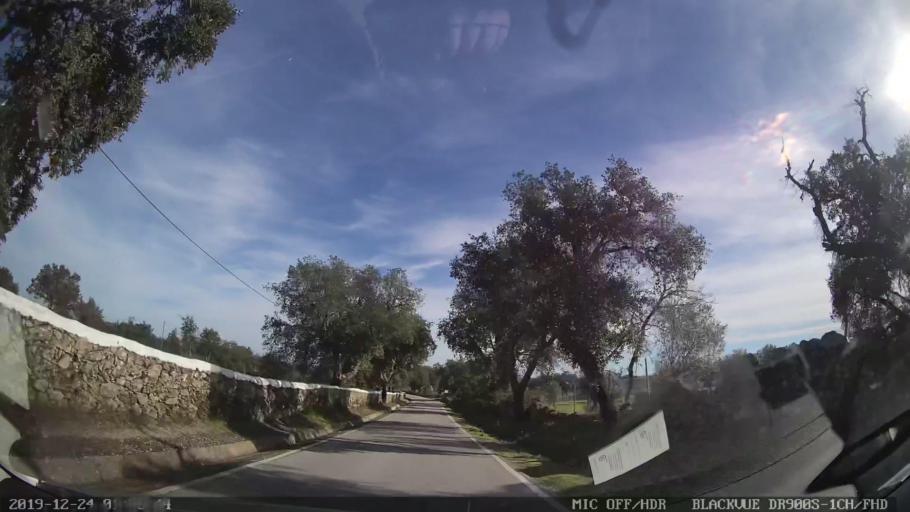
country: PT
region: Portalegre
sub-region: Nisa
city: Nisa
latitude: 39.4851
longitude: -7.7314
